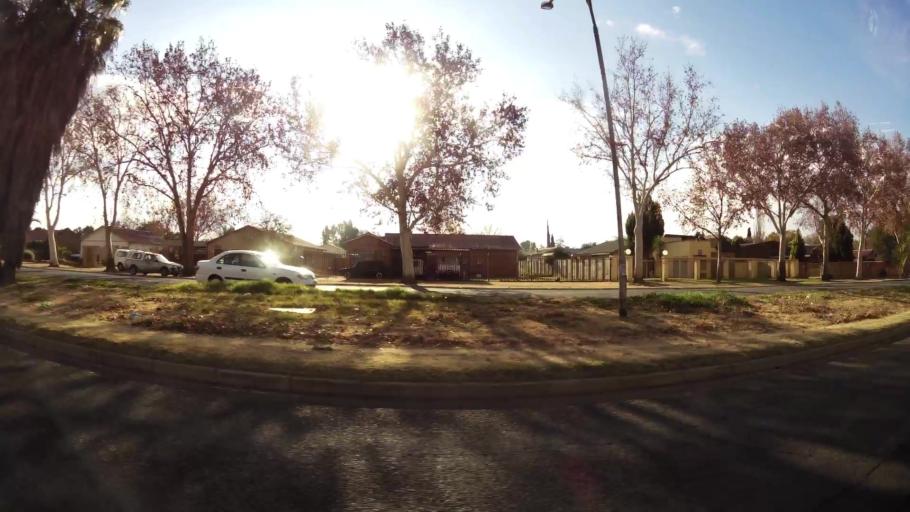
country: ZA
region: Orange Free State
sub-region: Lejweleputswa District Municipality
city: Welkom
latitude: -27.9892
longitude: 26.7534
